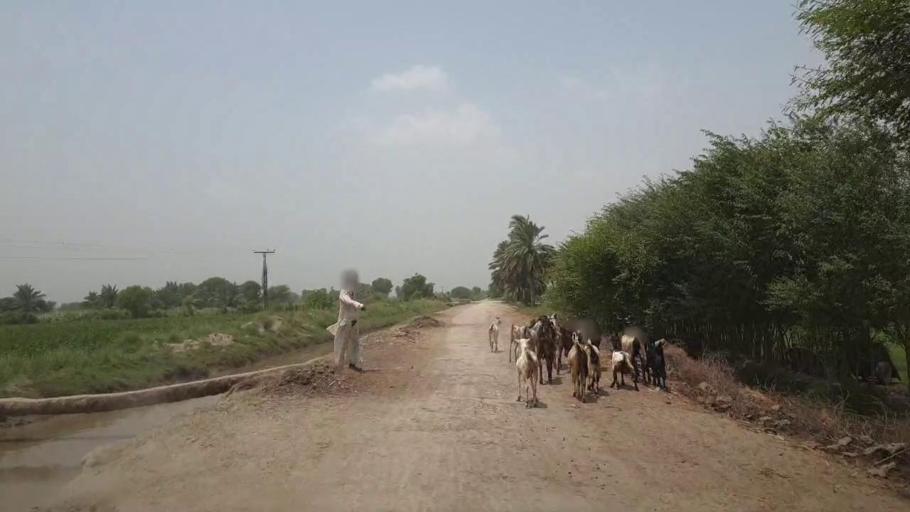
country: PK
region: Sindh
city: Sobhadero
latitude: 27.4363
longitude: 68.4003
